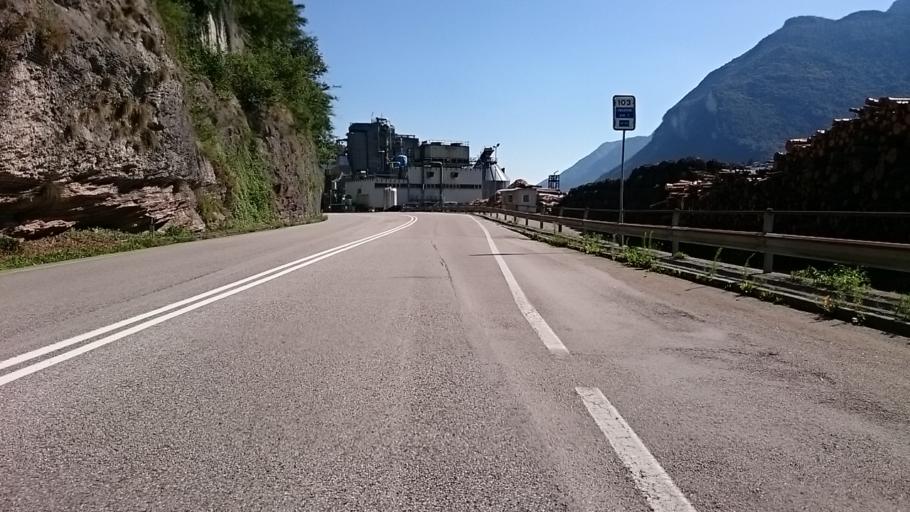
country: IT
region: Veneto
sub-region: Provincia di Belluno
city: Longarone
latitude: 46.2721
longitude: 12.3090
